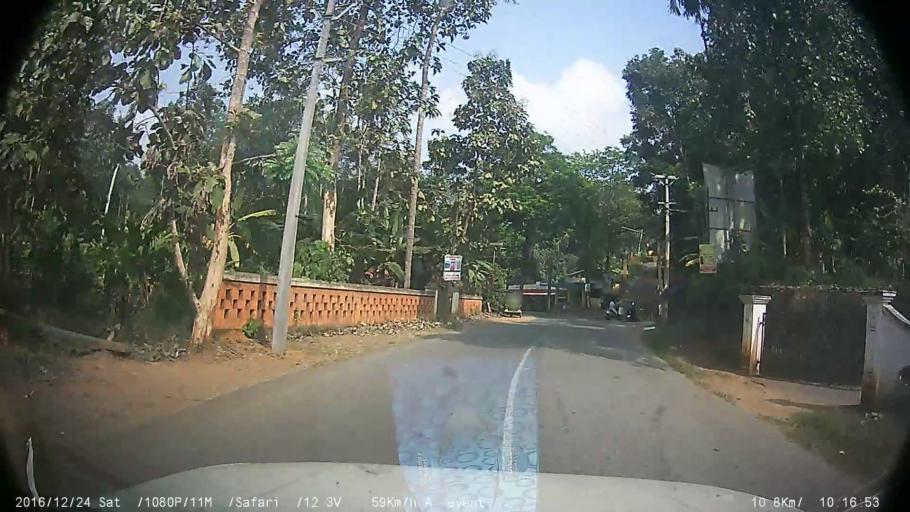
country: IN
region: Kerala
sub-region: Kottayam
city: Palackattumala
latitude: 9.8197
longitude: 76.6090
